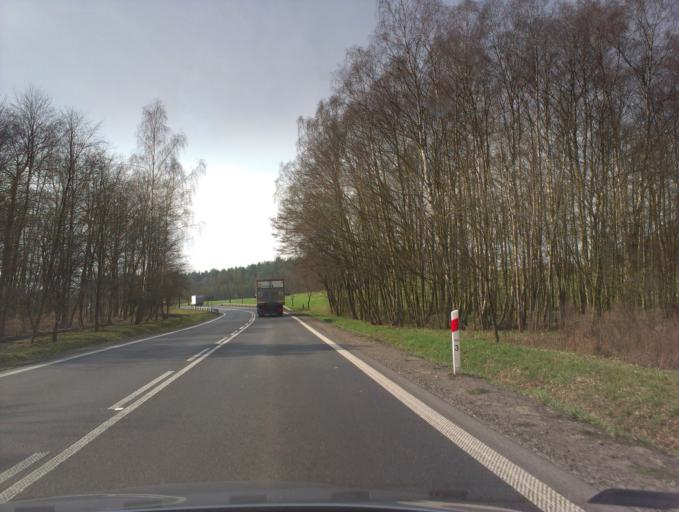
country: PL
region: Greater Poland Voivodeship
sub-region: Powiat zlotowski
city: Jastrowie
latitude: 53.4610
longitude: 16.8543
